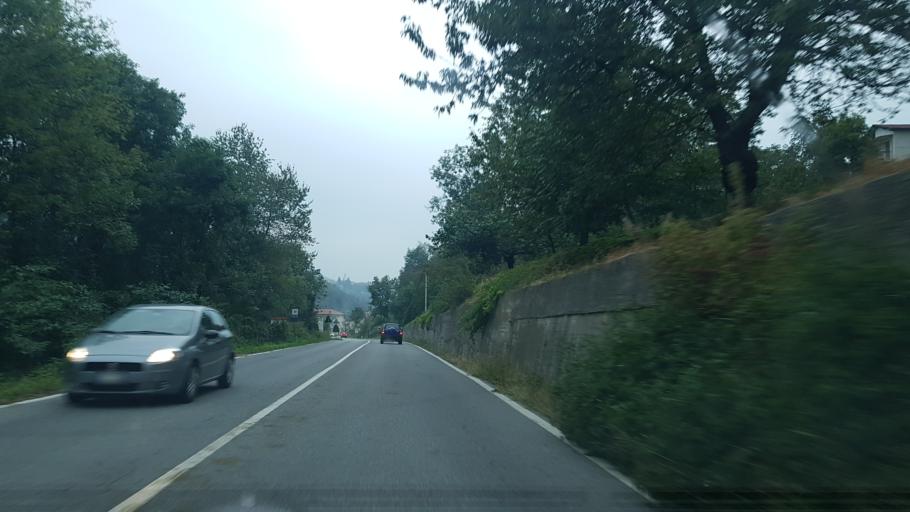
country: IT
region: Piedmont
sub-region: Provincia di Cuneo
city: Frabosa Sottana
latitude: 44.3261
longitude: 7.7980
